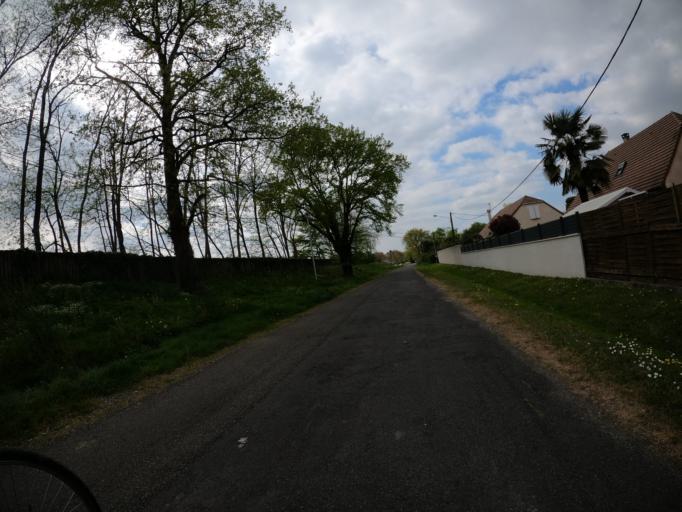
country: FR
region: Aquitaine
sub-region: Departement des Pyrenees-Atlantiques
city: Lons
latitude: 43.3204
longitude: -0.3889
